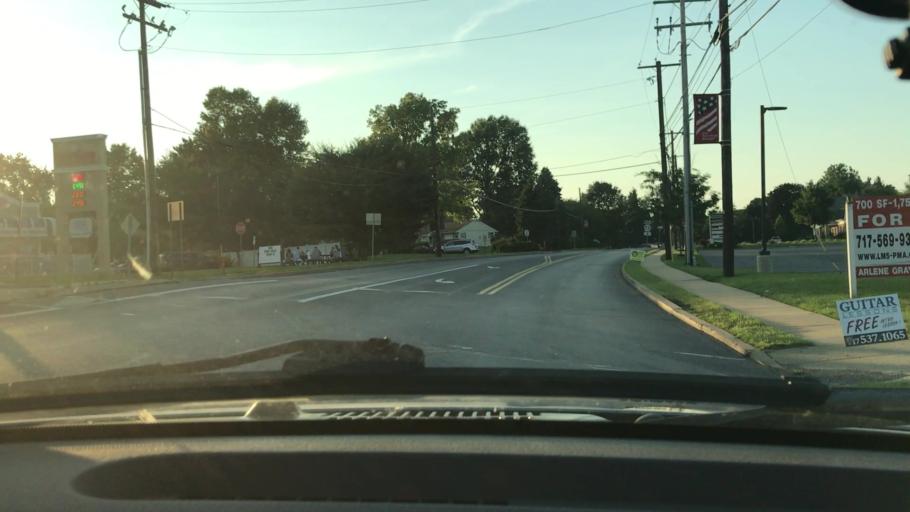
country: US
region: Pennsylvania
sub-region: Lancaster County
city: East Petersburg
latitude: 40.0936
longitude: -76.3506
